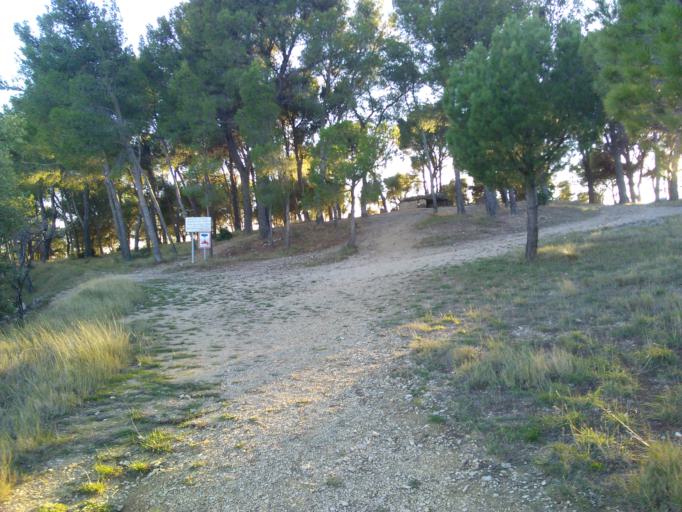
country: FR
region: Languedoc-Roussillon
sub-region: Departement de l'Aude
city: Pepieux
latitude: 43.3132
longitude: 2.6801
